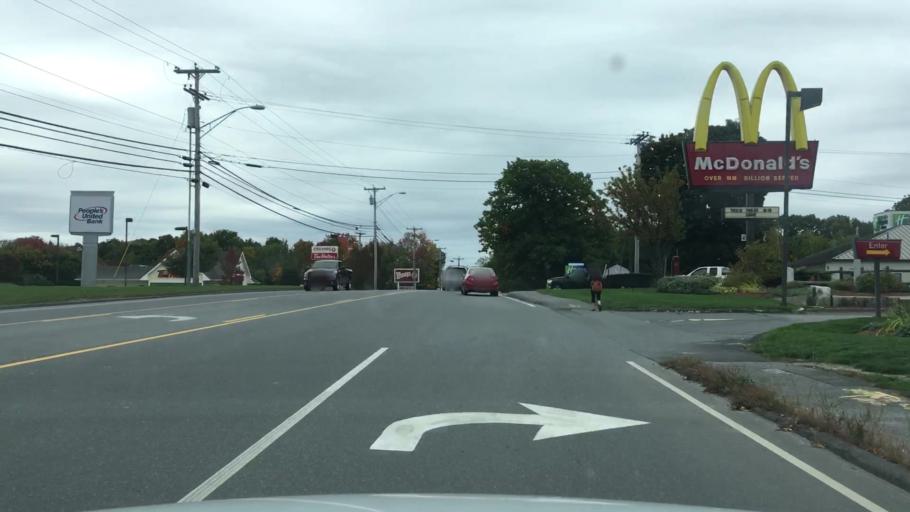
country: US
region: Maine
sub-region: Kennebec County
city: Waterville
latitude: 44.5666
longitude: -69.6378
